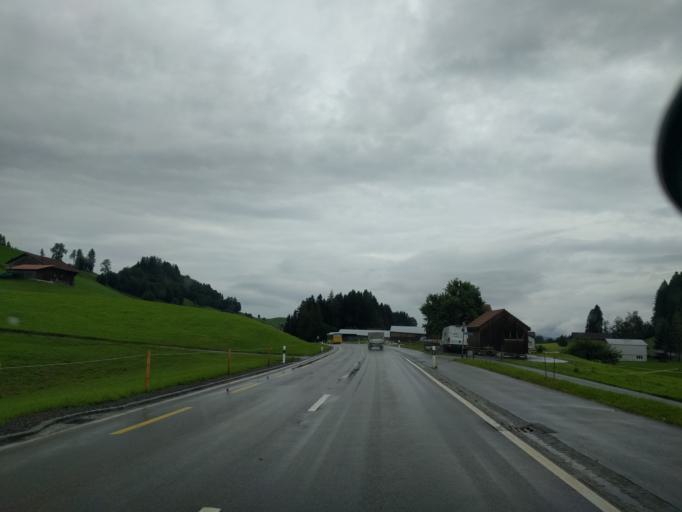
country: CH
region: Appenzell Ausserrhoden
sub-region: Bezirk Hinterland
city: Schwellbrunn
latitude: 47.3472
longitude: 9.2648
